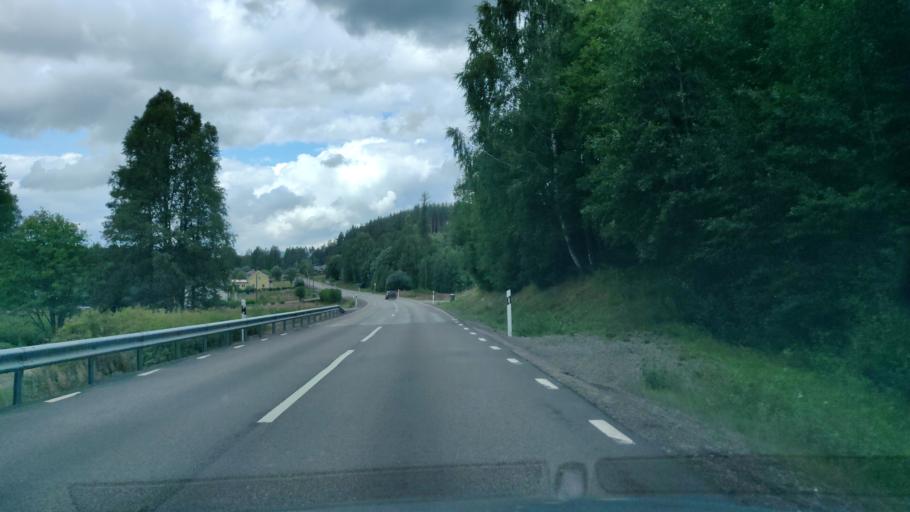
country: SE
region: Vaermland
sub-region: Torsby Kommun
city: Torsby
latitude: 60.5834
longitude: 13.0810
